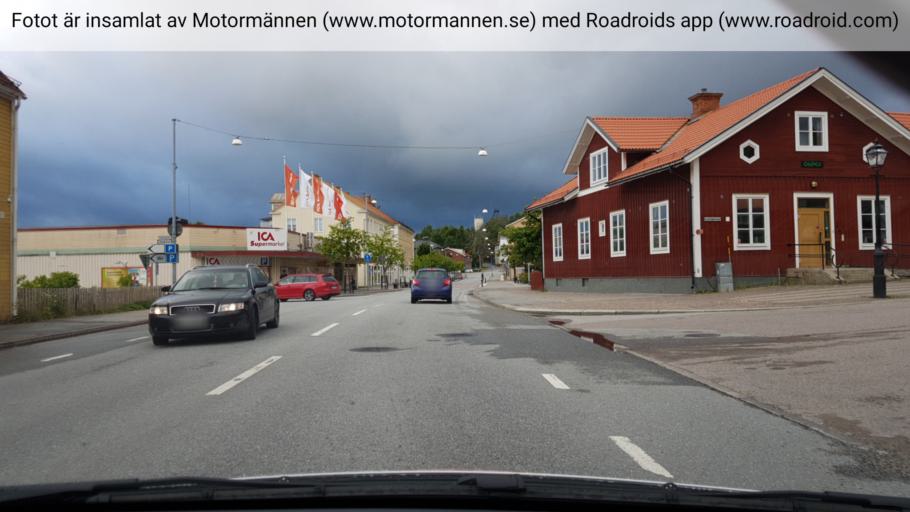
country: SE
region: OErebro
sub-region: Ljusnarsbergs Kommun
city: Kopparberg
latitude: 59.8751
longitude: 14.9983
